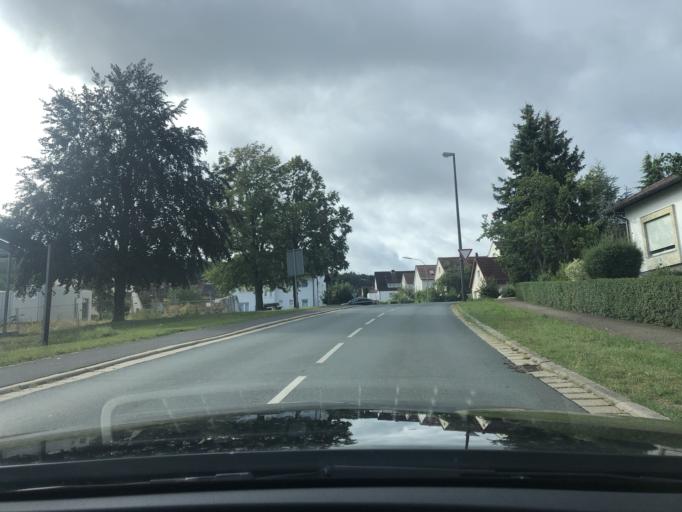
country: DE
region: Bavaria
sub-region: Regierungsbezirk Unterfranken
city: Rentweinsdorf
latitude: 50.0938
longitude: 10.8010
